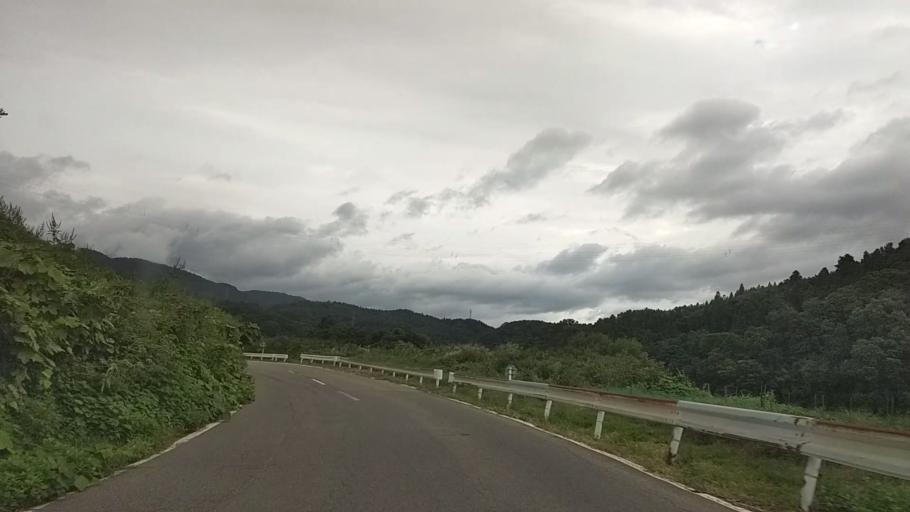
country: JP
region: Nagano
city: Nakano
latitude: 36.7950
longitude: 138.3457
